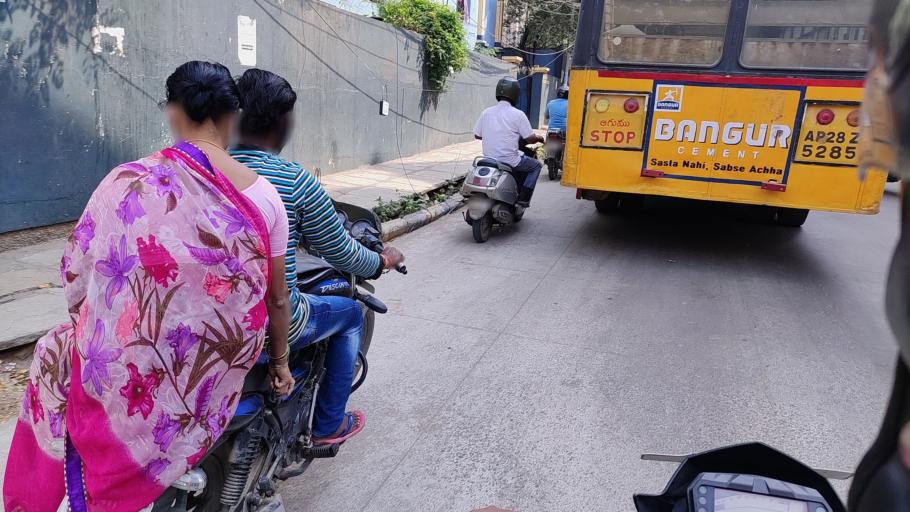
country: IN
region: Telangana
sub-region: Hyderabad
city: Hyderabad
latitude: 17.4312
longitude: 78.4386
